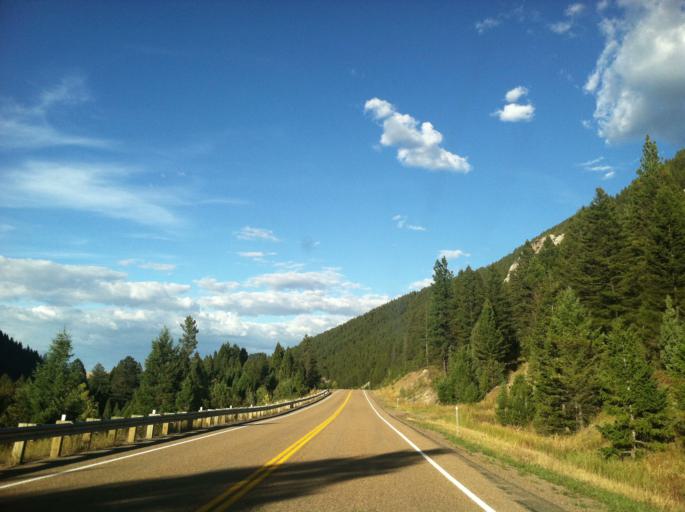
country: US
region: Montana
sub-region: Granite County
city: Philipsburg
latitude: 46.4491
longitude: -113.2473
